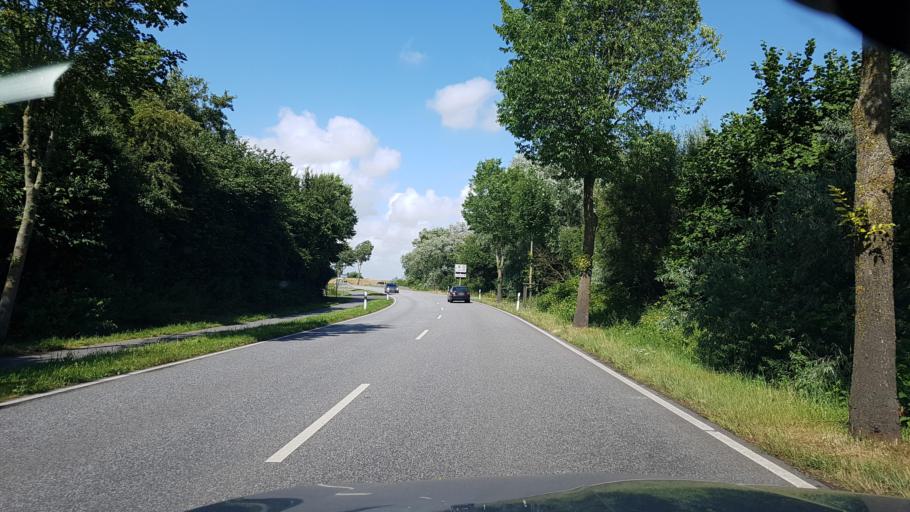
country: DE
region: Schleswig-Holstein
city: Busumer Deichhausen
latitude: 54.1312
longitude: 8.8749
